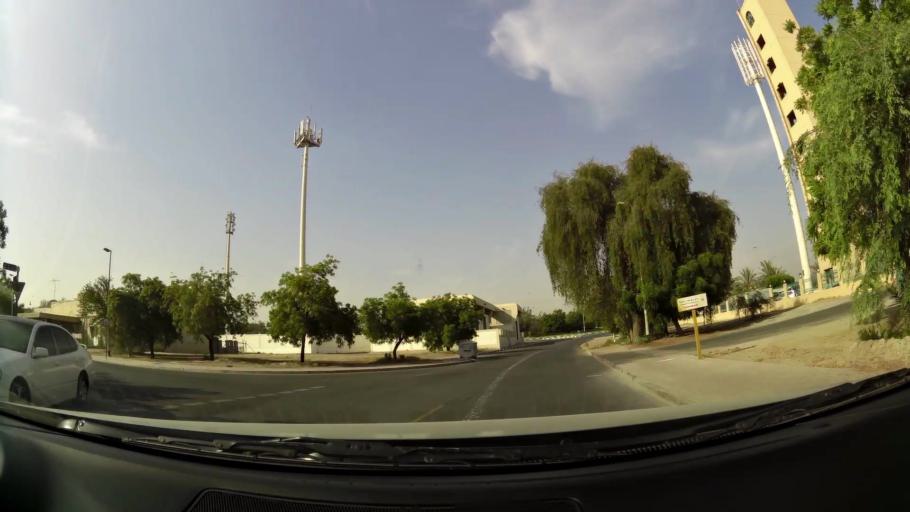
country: AE
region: Ash Shariqah
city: Sharjah
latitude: 25.2228
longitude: 55.3780
